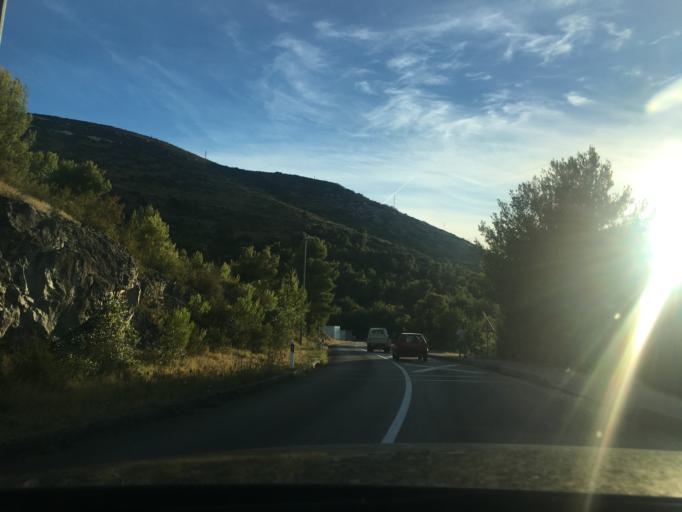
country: HR
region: Splitsko-Dalmatinska
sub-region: Grad Vis
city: Vis
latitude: 43.0564
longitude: 16.1948
